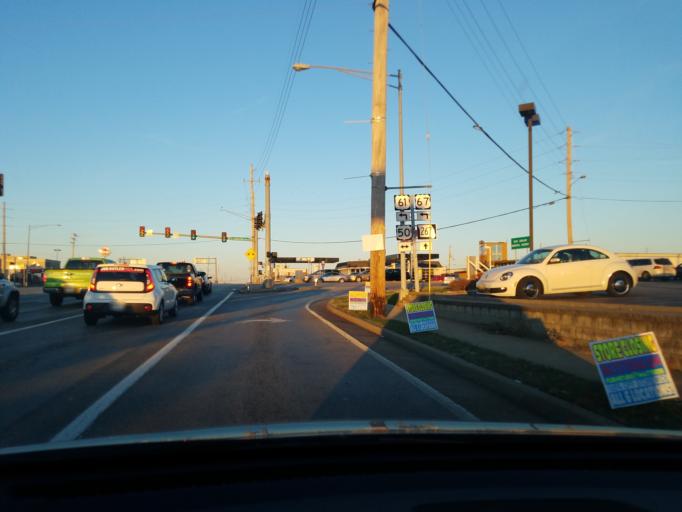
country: US
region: Missouri
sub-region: Saint Louis County
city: Mehlville
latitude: 38.5055
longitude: -90.3263
